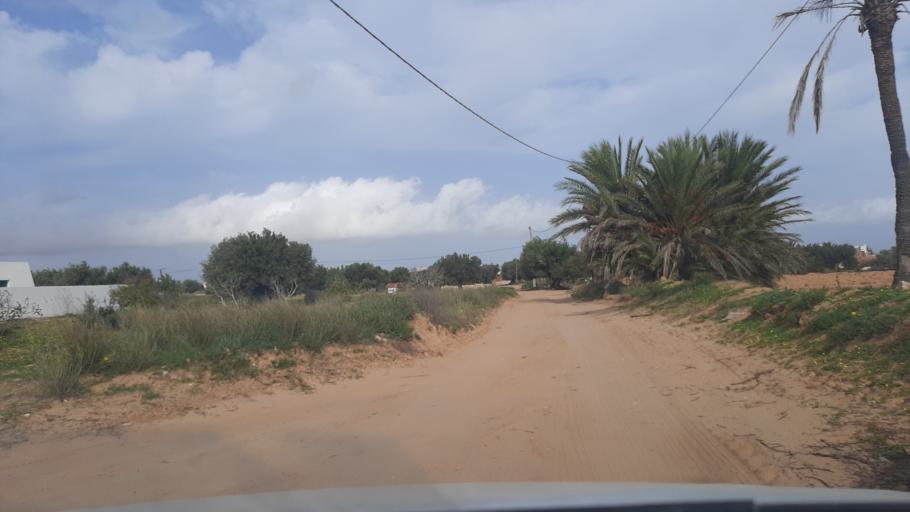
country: TN
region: Madanin
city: Midoun
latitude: 33.8053
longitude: 11.0246
